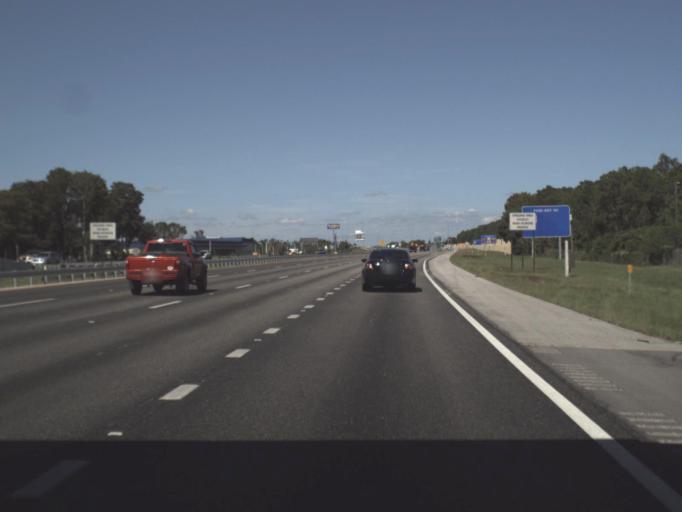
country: US
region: Florida
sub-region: Lee County
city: Tice
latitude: 26.6709
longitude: -81.7994
